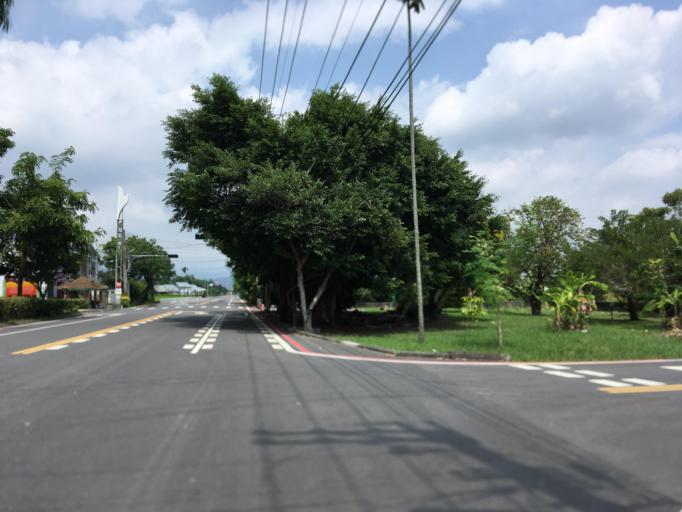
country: TW
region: Taiwan
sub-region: Yilan
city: Yilan
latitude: 24.6791
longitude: 121.6890
